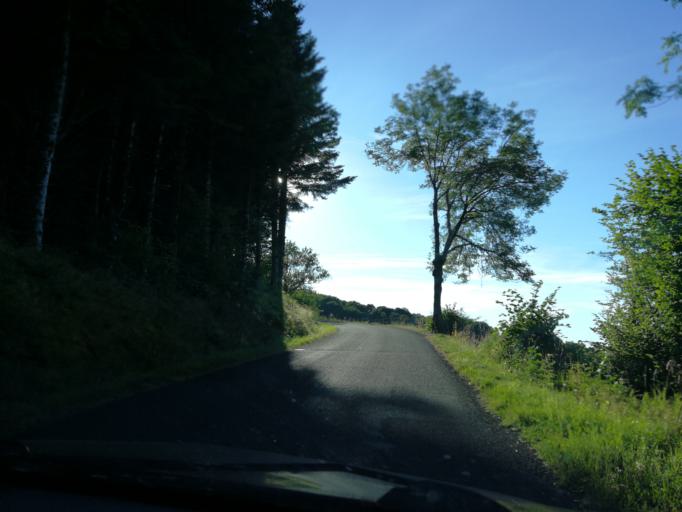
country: FR
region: Auvergne
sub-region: Departement du Cantal
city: Vic-sur-Cere
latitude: 45.0782
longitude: 2.5662
